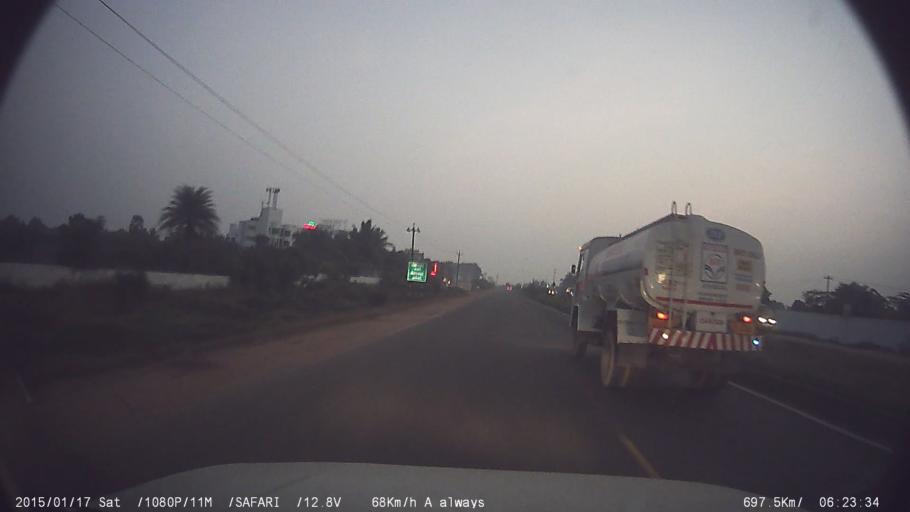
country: IN
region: Tamil Nadu
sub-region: Kancheepuram
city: Sriperumbudur
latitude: 12.9123
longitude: 79.8522
